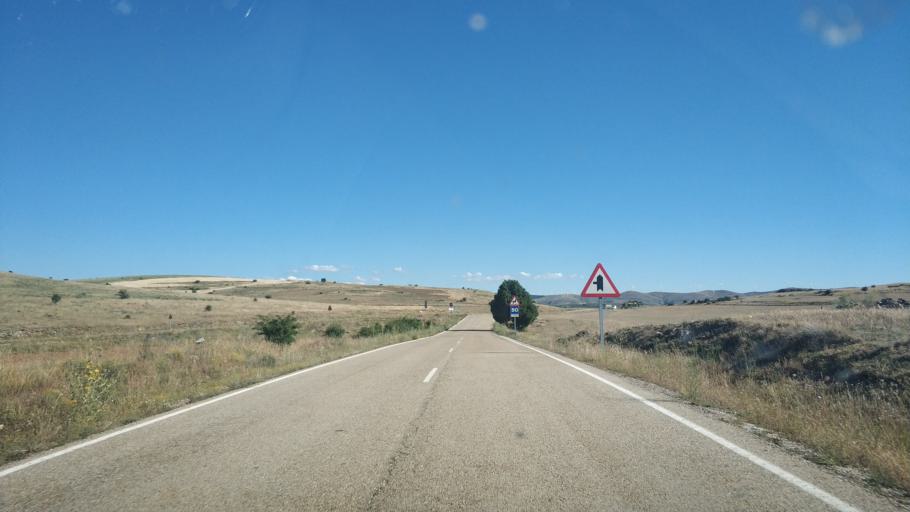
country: ES
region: Castille and Leon
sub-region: Provincia de Soria
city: Montejo de Tiermes
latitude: 41.3756
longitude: -3.1915
